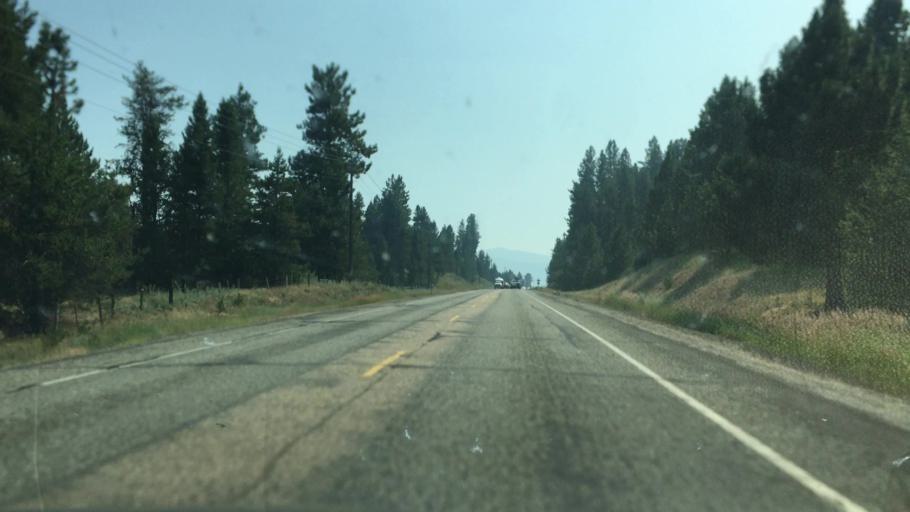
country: US
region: Idaho
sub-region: Valley County
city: Cascade
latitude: 44.3706
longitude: -116.0170
